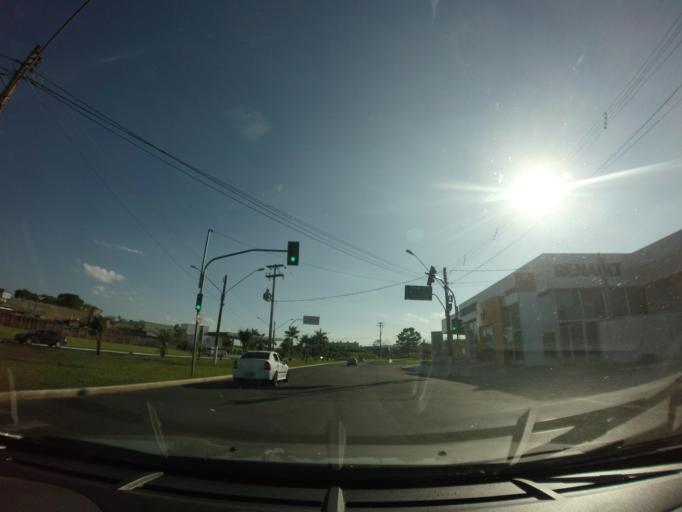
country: BR
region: Sao Paulo
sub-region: Rio Claro
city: Rio Claro
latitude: -22.4178
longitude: -47.5756
